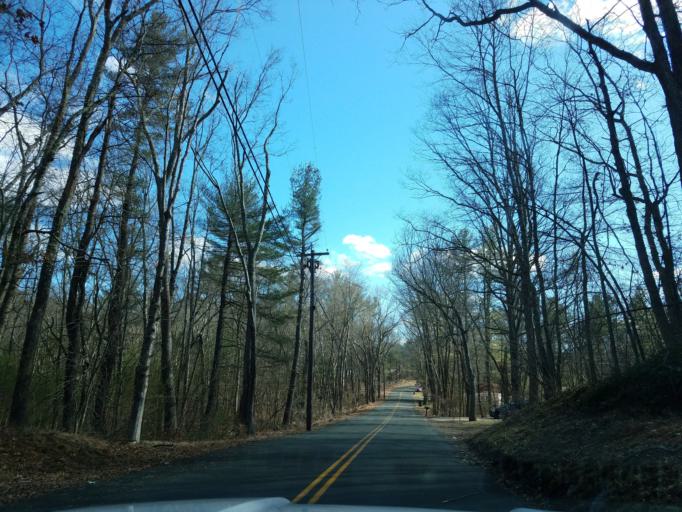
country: US
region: Connecticut
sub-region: Windham County
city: North Grosvenor Dale
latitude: 42.0115
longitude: -71.8715
